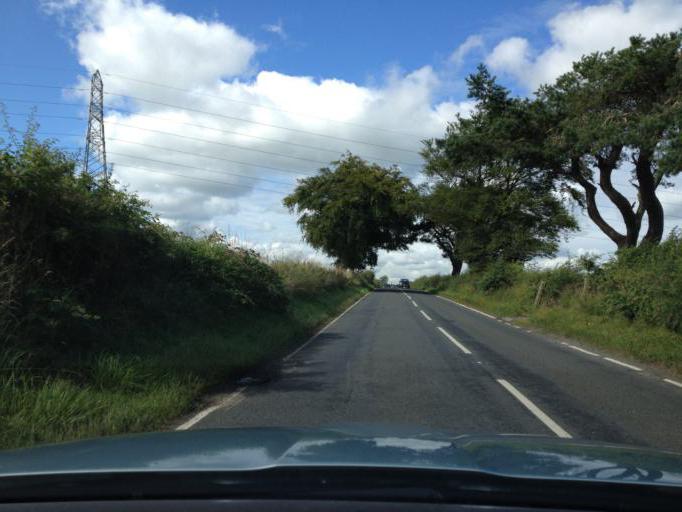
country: GB
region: Scotland
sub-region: West Lothian
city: Armadale
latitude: 55.9312
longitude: -3.7134
